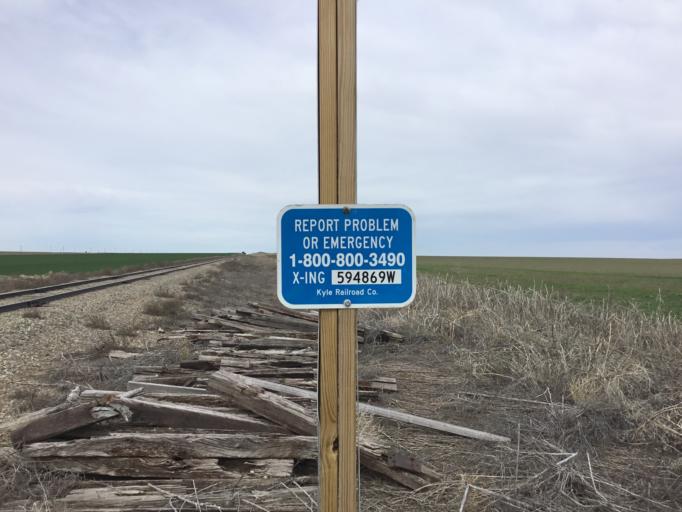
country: US
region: Kansas
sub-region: Sherman County
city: Goodland
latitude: 39.3385
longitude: -101.9118
